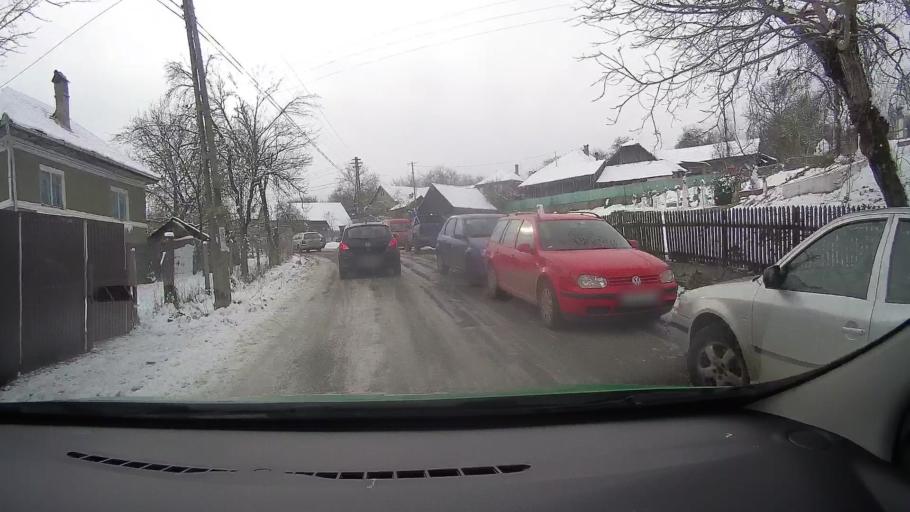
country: RO
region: Alba
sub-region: Comuna Almasu Mare
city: Almasu Mare
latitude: 46.0900
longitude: 23.1300
